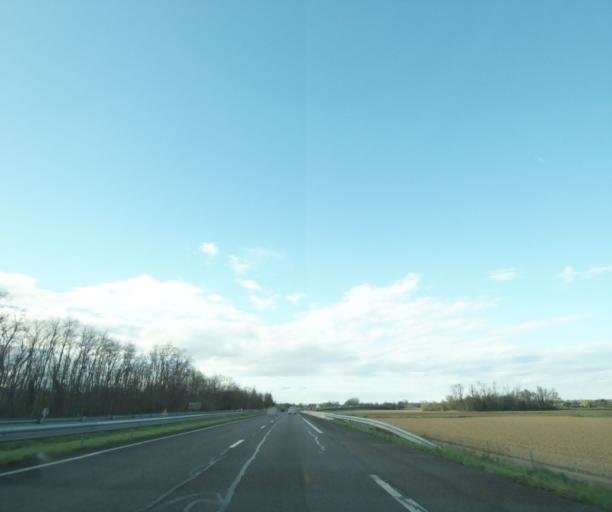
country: FR
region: Rhone-Alpes
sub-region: Departement du Rhone
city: Anse
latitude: 45.9198
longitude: 4.7258
